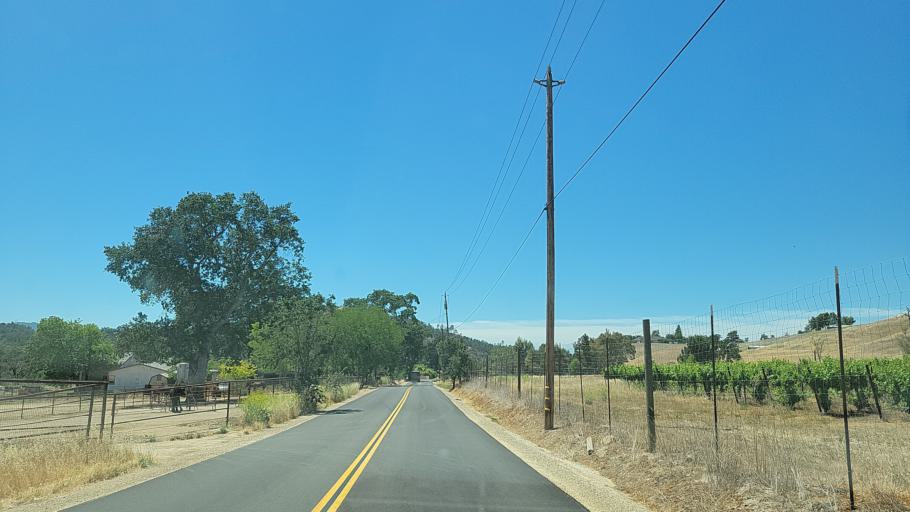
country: US
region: California
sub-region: San Luis Obispo County
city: Atascadero
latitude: 35.4869
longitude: -120.6346
